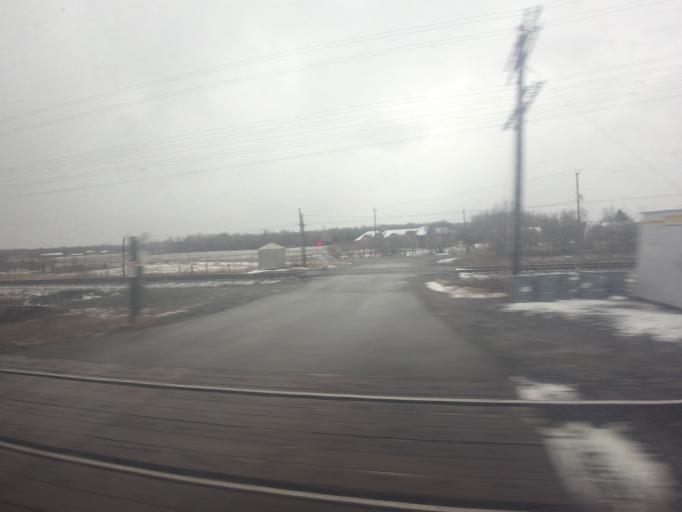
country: CA
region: Ontario
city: Quinte West
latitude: 44.0537
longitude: -77.6876
